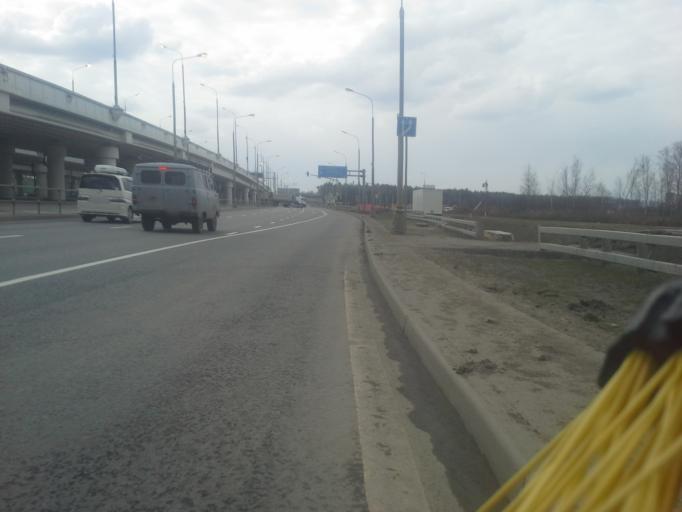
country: RU
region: Moskovskaya
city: Mosrentgen
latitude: 55.5967
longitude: 37.4164
